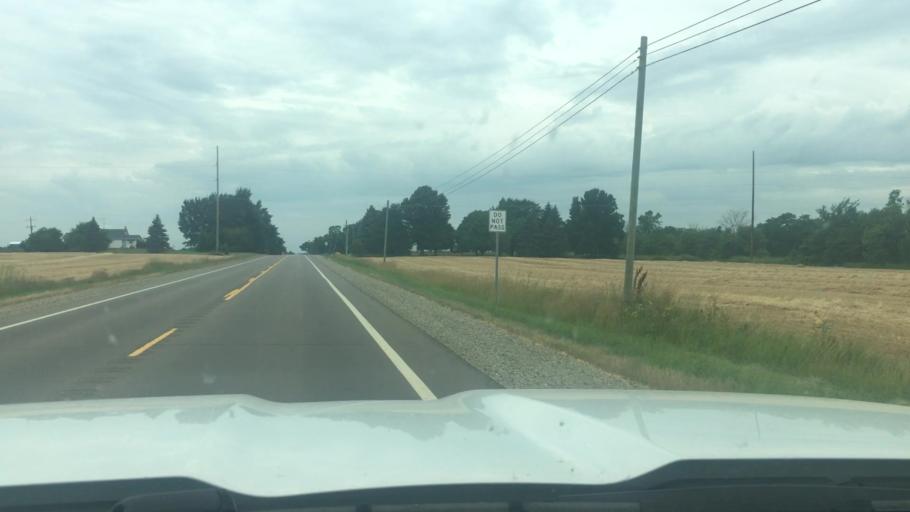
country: US
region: Michigan
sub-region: Clinton County
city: Fowler
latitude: 43.0018
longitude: -84.7619
